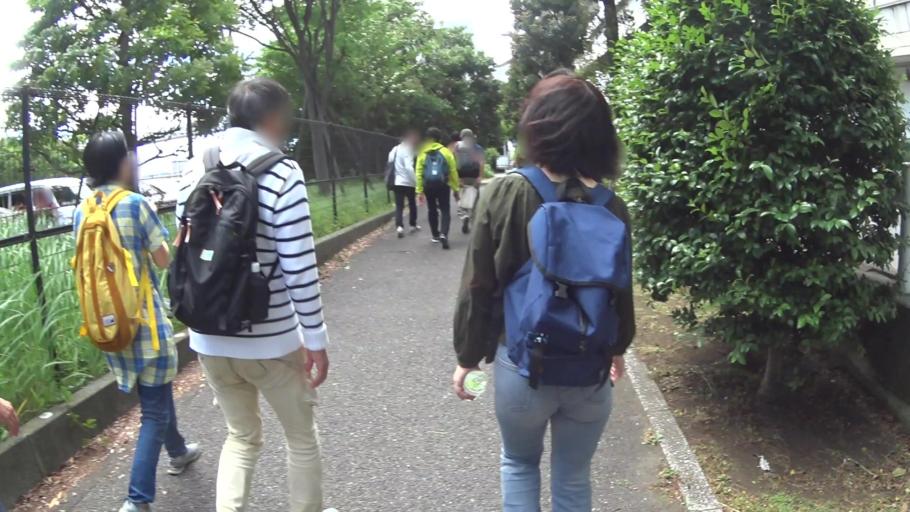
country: JP
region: Tokyo
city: Tokyo
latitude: 35.6400
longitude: 139.7604
